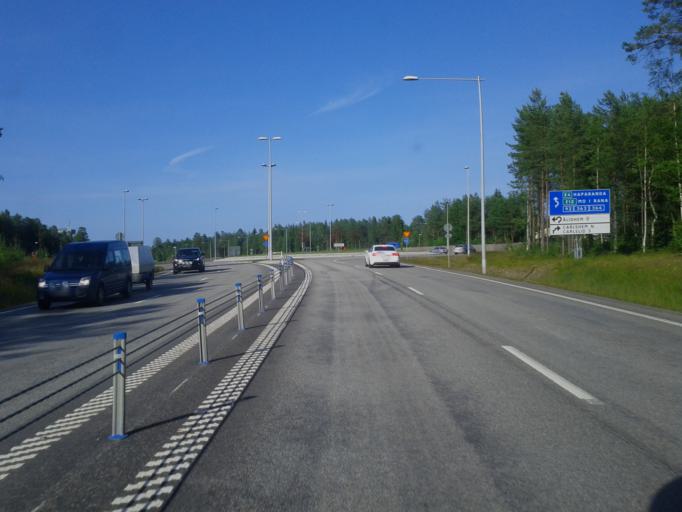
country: SE
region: Vaesterbotten
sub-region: Umea Kommun
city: Umea
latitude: 63.8050
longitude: 20.3198
